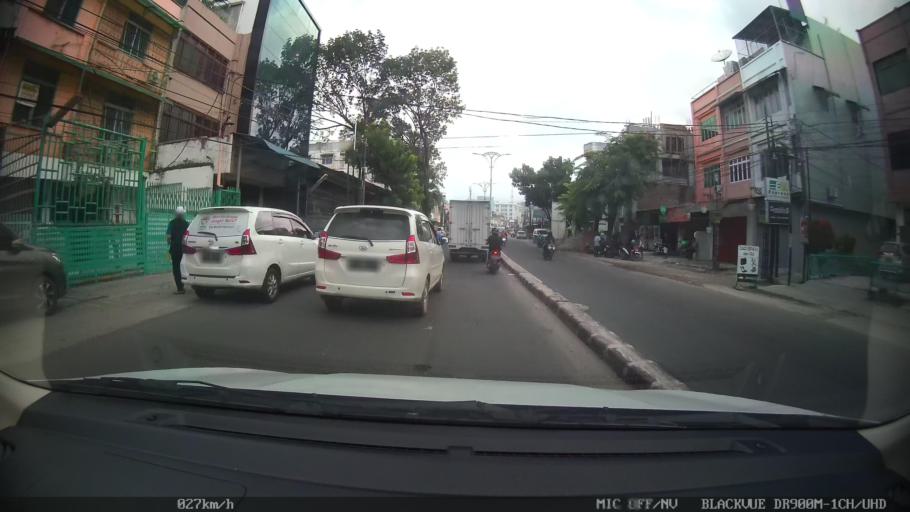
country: ID
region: North Sumatra
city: Medan
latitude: 3.6115
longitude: 98.6739
